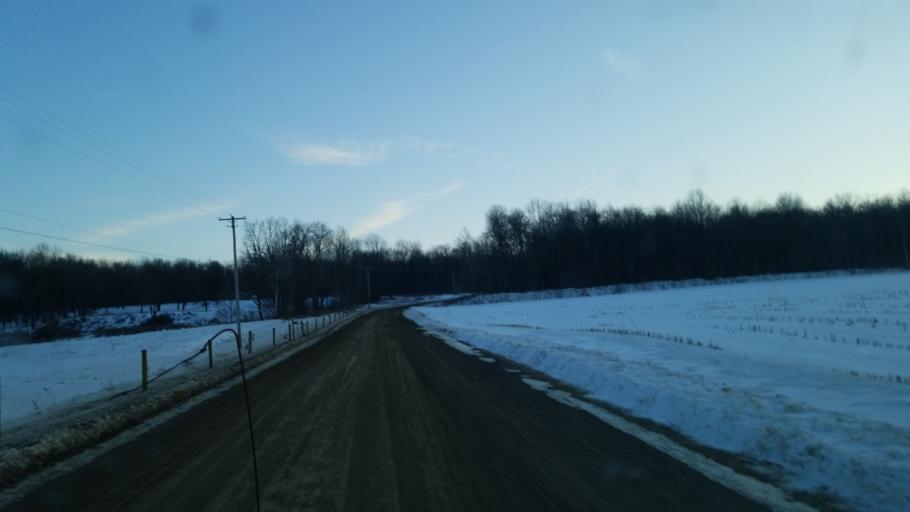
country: US
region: Pennsylvania
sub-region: Tioga County
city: Westfield
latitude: 42.0096
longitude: -77.6826
